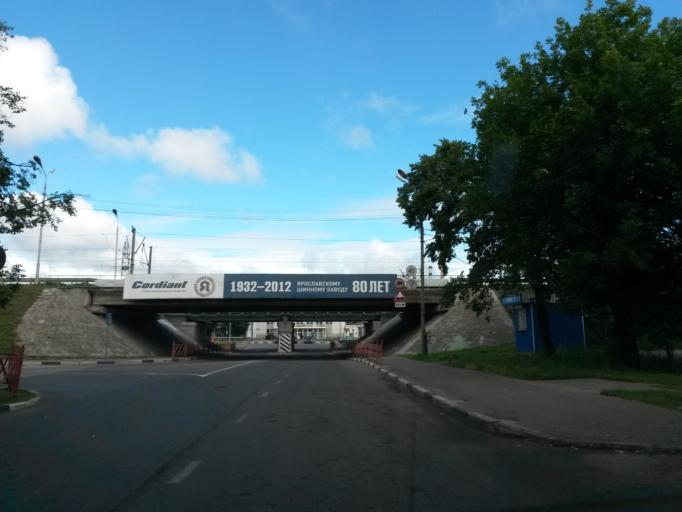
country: RU
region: Jaroslavl
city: Yaroslavl
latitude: 57.6432
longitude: 39.8744
